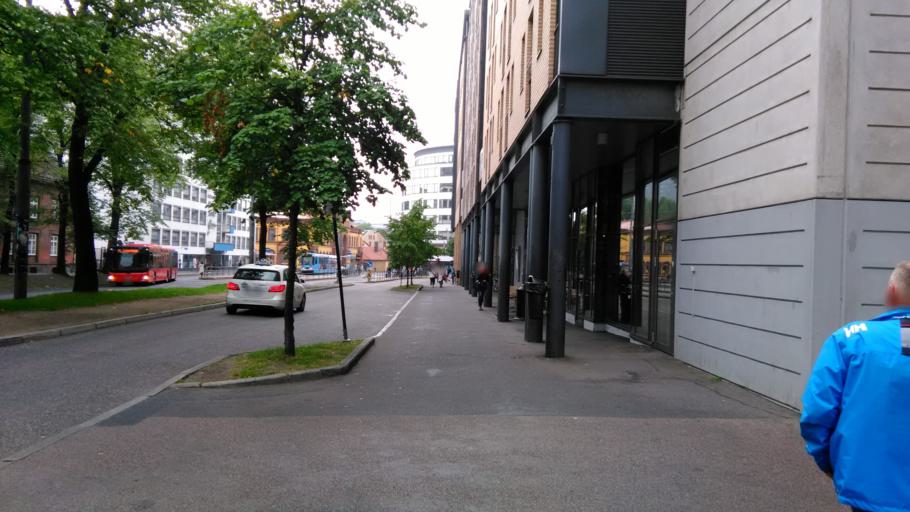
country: NO
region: Oslo
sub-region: Oslo
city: Oslo
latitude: 59.9171
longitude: 10.7580
